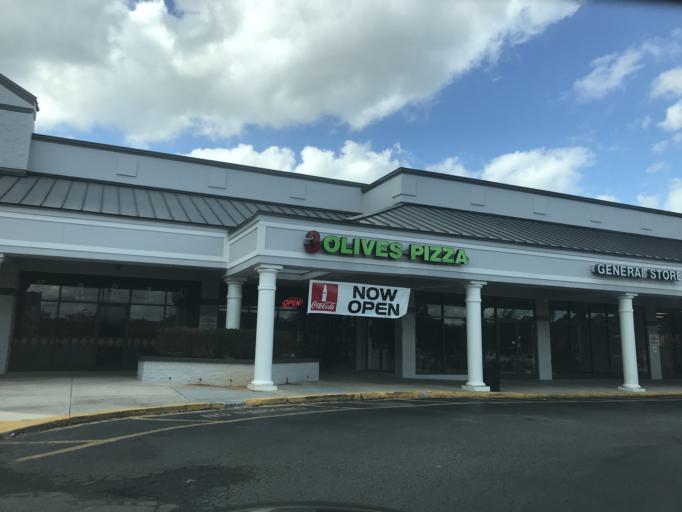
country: US
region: North Carolina
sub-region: Wake County
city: Garner
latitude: 35.7231
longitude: -78.6555
